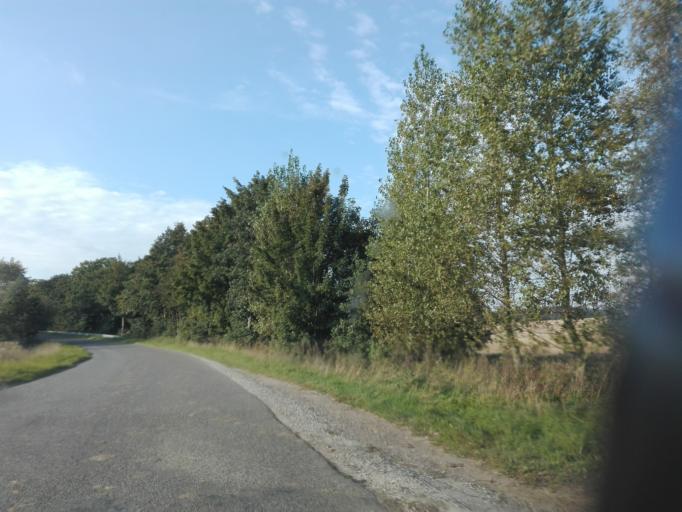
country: DK
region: Central Jutland
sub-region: Arhus Kommune
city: Malling
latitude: 56.0118
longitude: 10.1768
